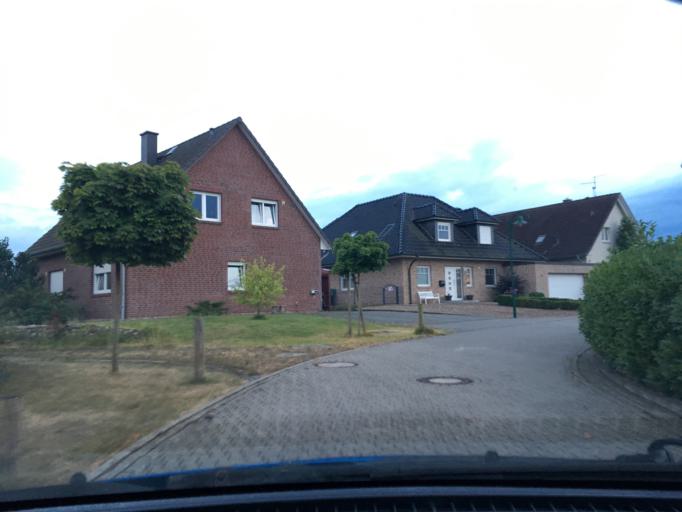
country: DE
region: Lower Saxony
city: Melbeck
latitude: 53.1748
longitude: 10.4060
